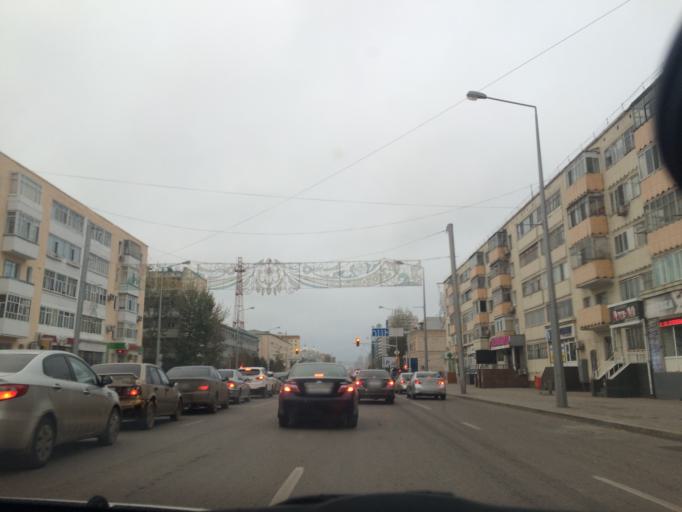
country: KZ
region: Astana Qalasy
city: Astana
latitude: 51.1734
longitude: 71.4068
